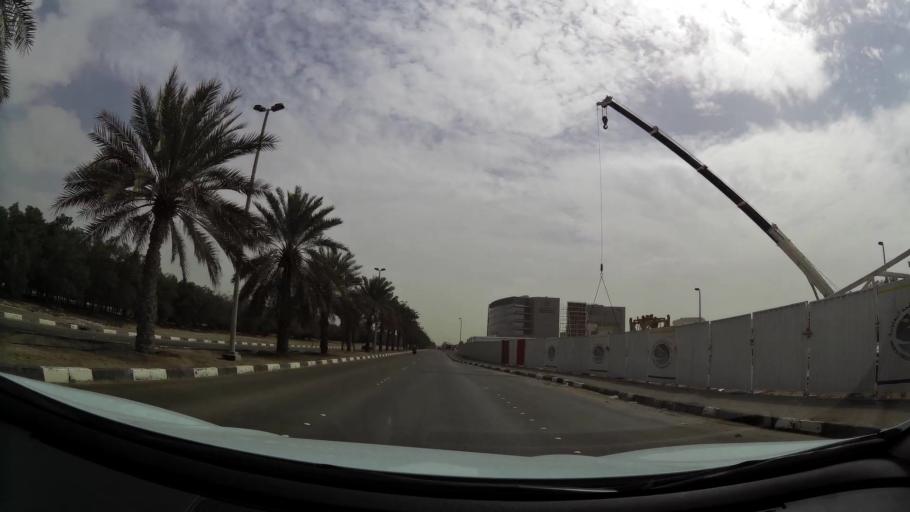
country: AE
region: Abu Dhabi
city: Abu Dhabi
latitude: 24.3983
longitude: 54.4980
